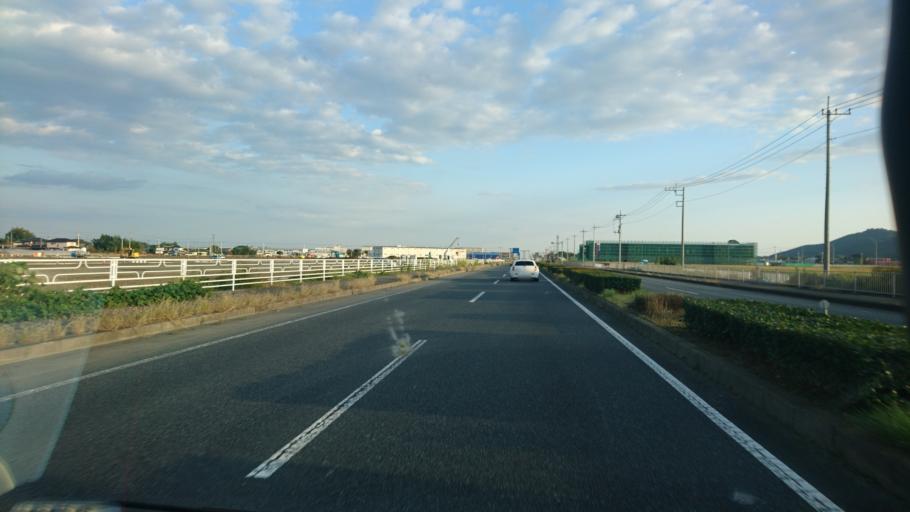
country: JP
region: Gunma
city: Ota
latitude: 36.3522
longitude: 139.3772
